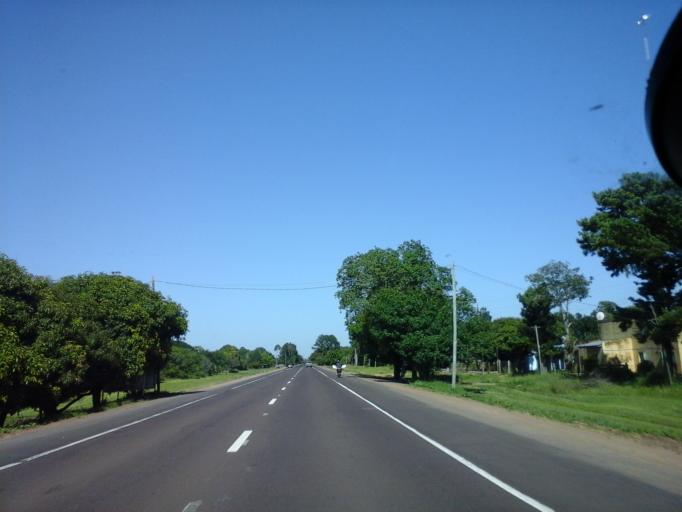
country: AR
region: Corrientes
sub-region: Departamento de San Cosme
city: San Cosme
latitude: -27.3686
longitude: -58.4100
